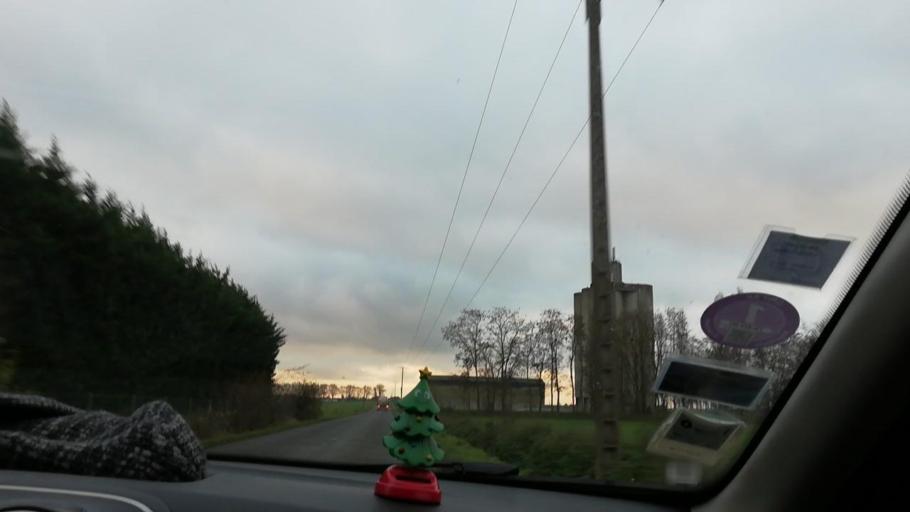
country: FR
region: Ile-de-France
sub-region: Departement de Seine-et-Marne
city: Charny
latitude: 48.9690
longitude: 2.7525
